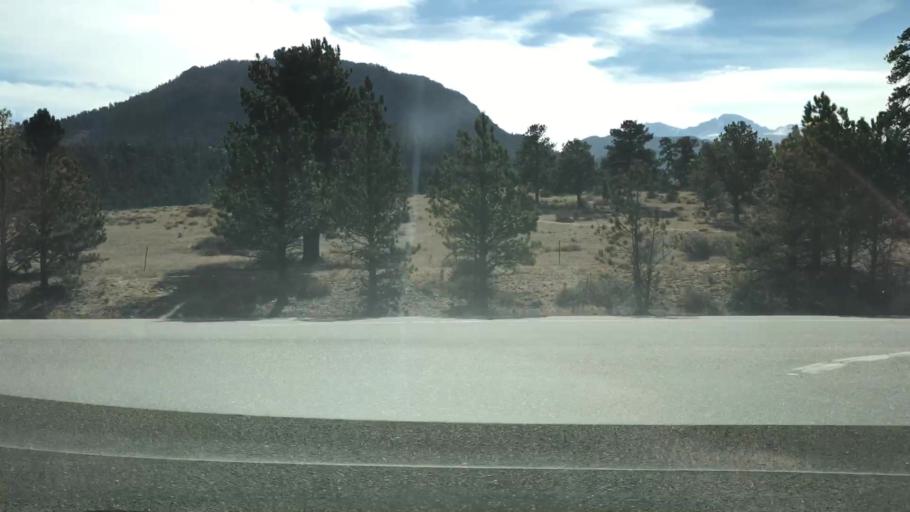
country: US
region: Colorado
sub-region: Larimer County
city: Estes Park
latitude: 40.3808
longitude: -105.5186
